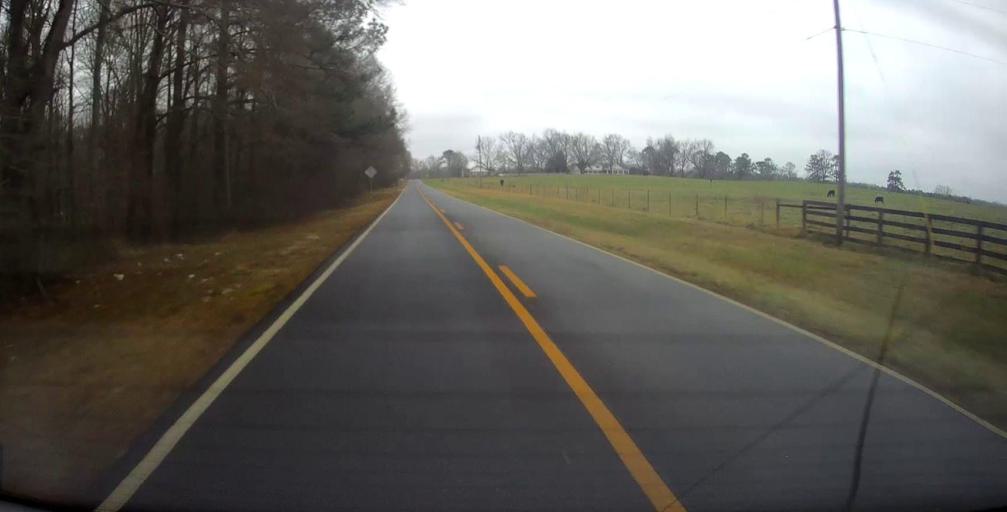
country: US
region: Georgia
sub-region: Pike County
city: Zebulon
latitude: 33.1126
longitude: -84.3669
